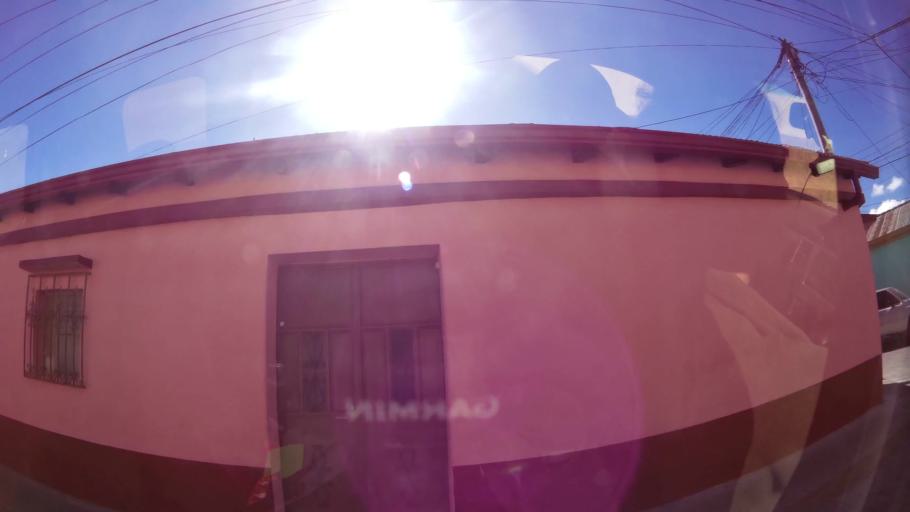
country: GT
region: Quetzaltenango
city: Quetzaltenango
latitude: 14.8354
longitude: -91.5103
